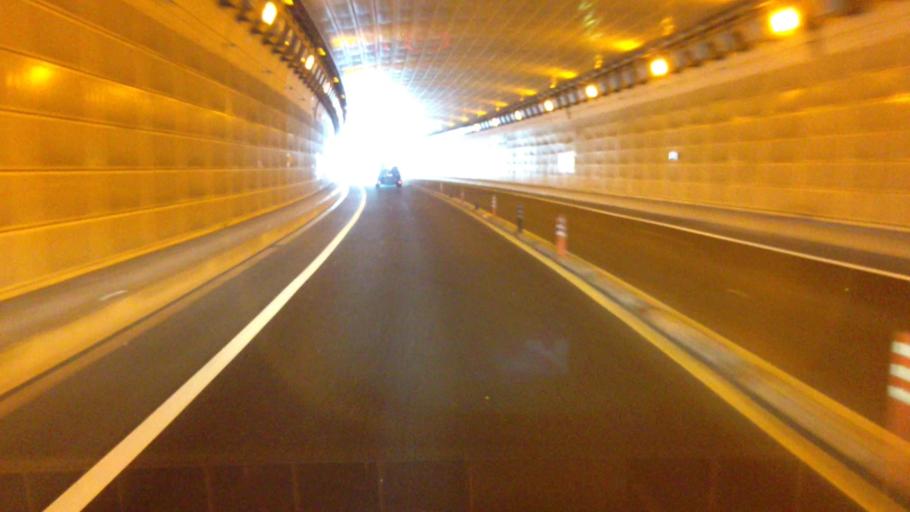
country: JP
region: Kanagawa
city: Yokosuka
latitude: 35.2224
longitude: 139.6368
